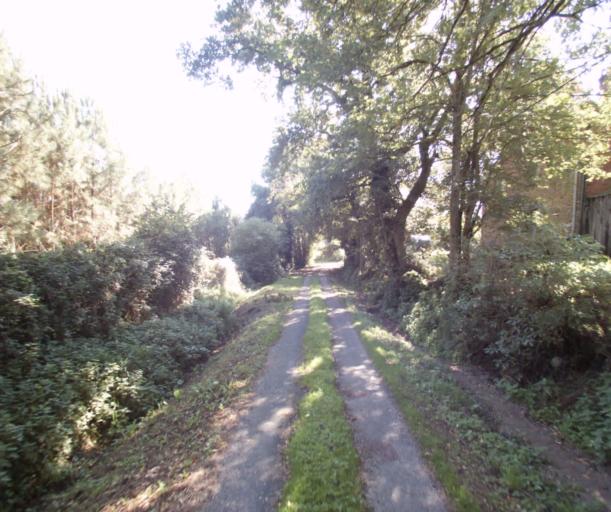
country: FR
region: Midi-Pyrenees
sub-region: Departement du Gers
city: Cazaubon
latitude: 43.9396
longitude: -0.0341
